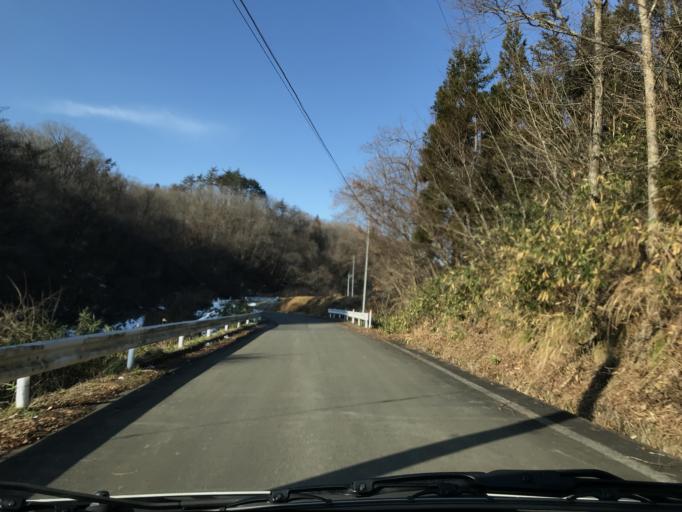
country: JP
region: Iwate
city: Ichinoseki
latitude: 38.9682
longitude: 141.0461
